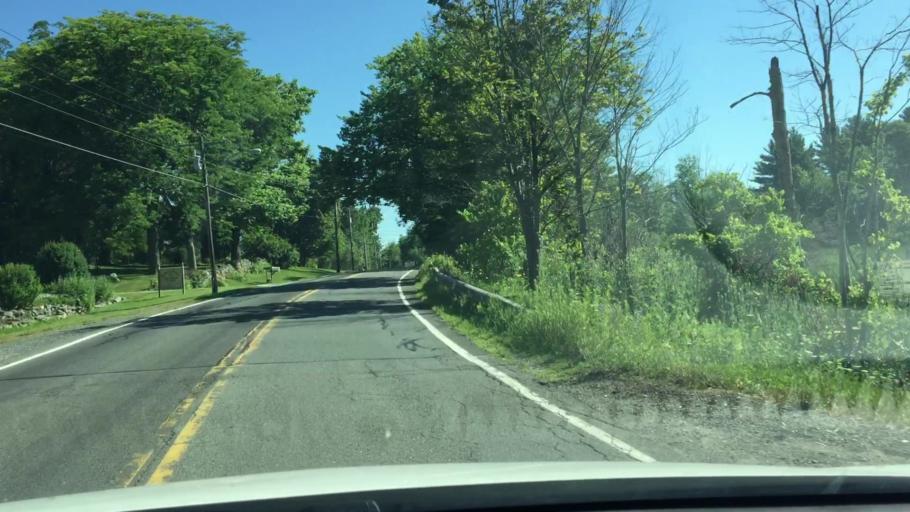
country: US
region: Massachusetts
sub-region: Berkshire County
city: Lenox
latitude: 42.4145
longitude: -73.3126
